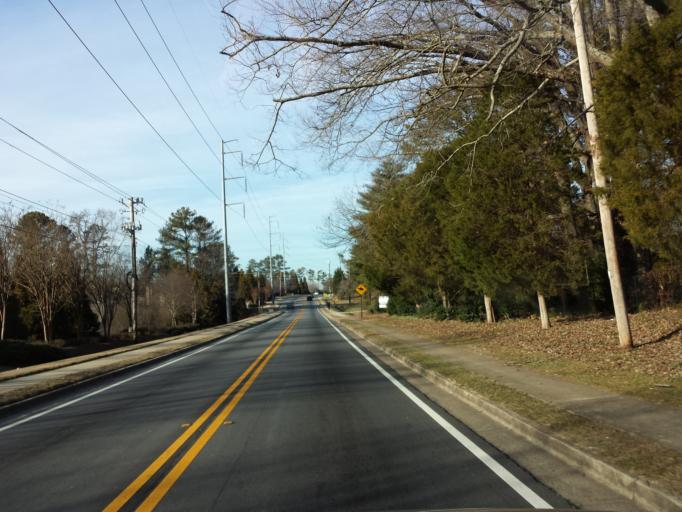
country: US
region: Georgia
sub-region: Cobb County
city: Marietta
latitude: 34.0084
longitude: -84.5470
